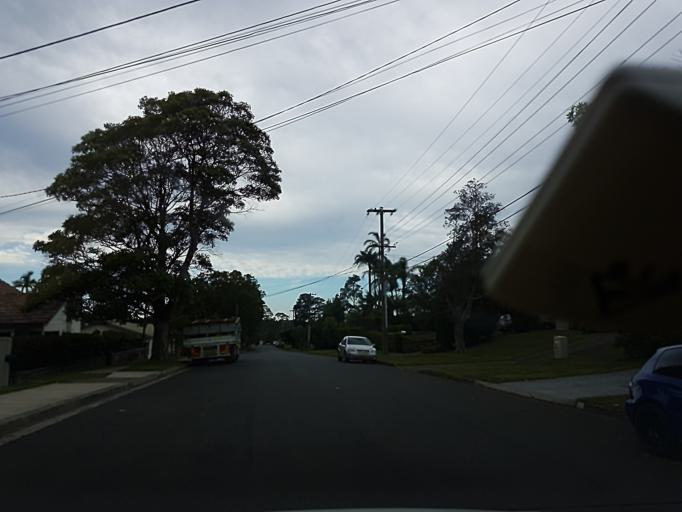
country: AU
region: New South Wales
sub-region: Warringah
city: Davidson
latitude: -33.7250
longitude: 151.2143
